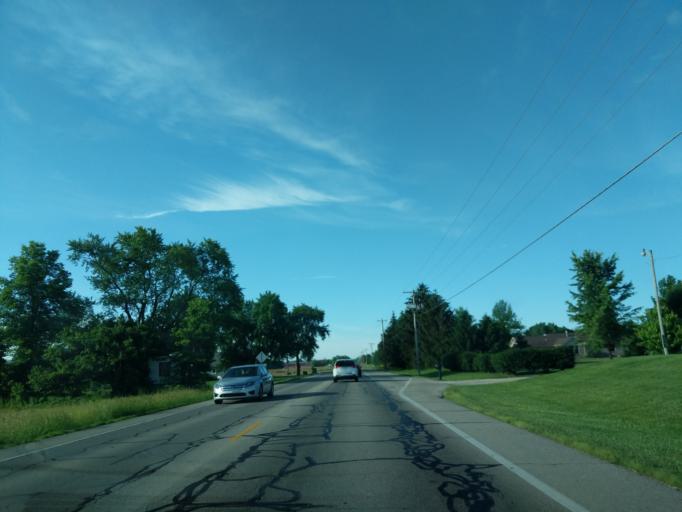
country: US
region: Indiana
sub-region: Hancock County
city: Greenfield
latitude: 39.8702
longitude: -85.7703
